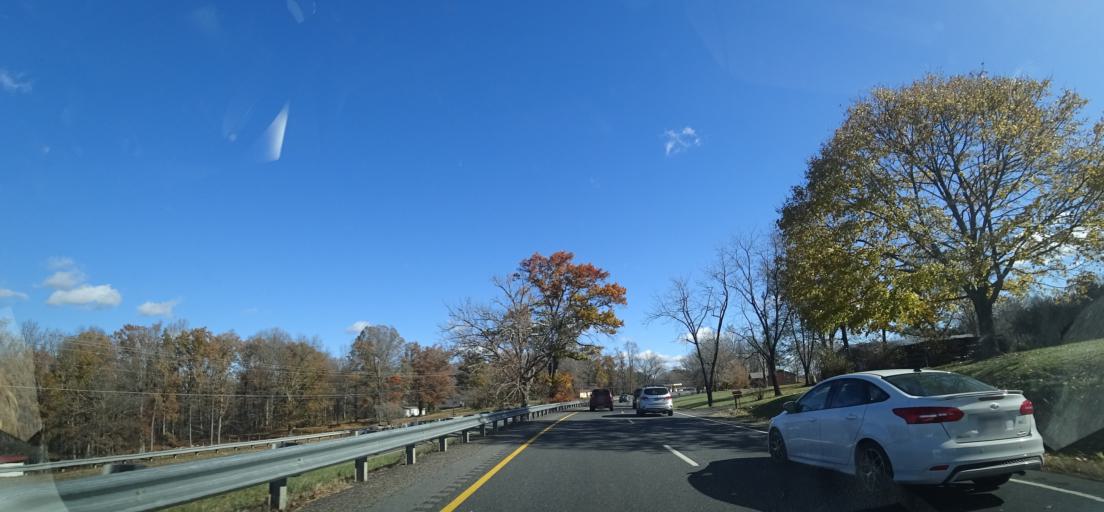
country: US
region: Virginia
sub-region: Culpeper County
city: Merrimac
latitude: 38.4563
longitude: -78.1206
